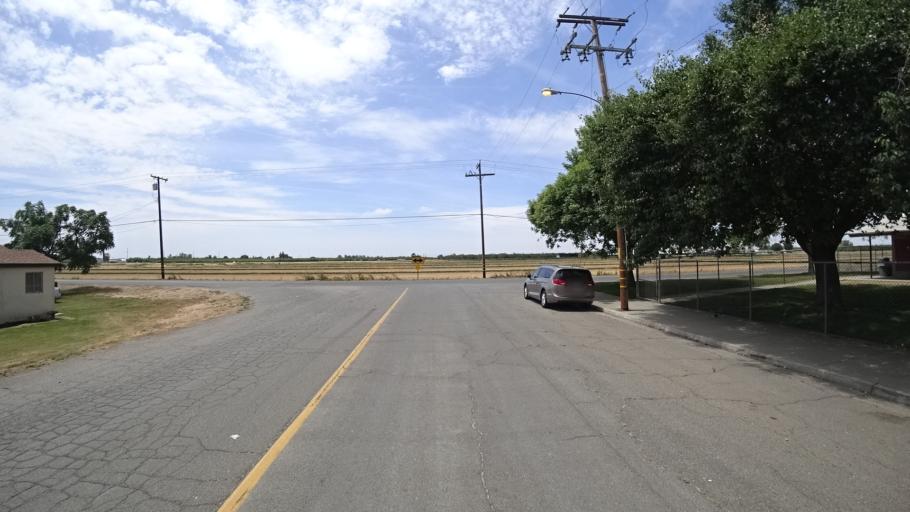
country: US
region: California
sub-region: Kings County
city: Armona
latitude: 36.3171
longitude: -119.7176
